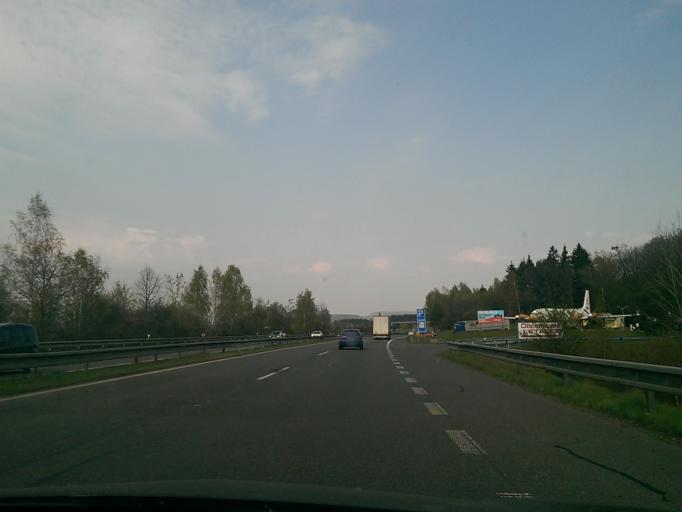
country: CZ
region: Central Bohemia
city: Bakov nad Jizerou
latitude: 50.4646
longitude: 14.9401
